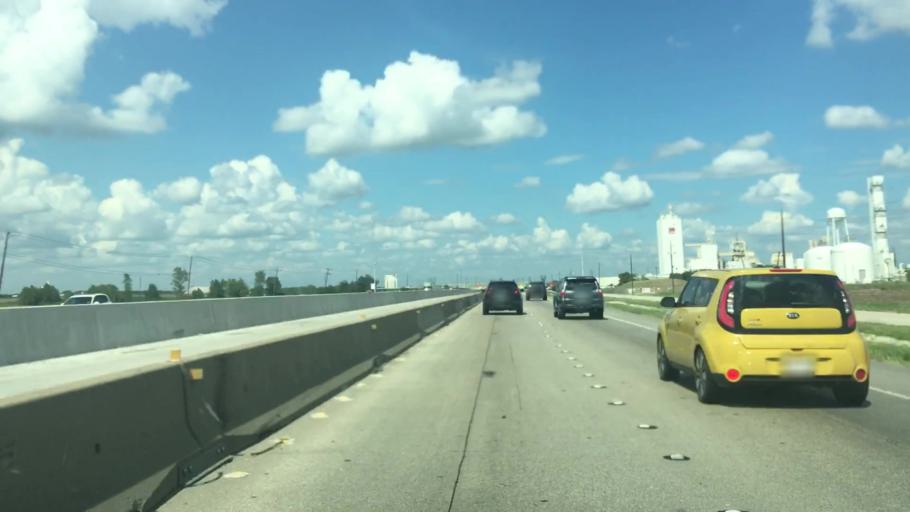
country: US
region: Texas
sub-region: Ellis County
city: Waxahachie
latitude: 32.4352
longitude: -96.8543
